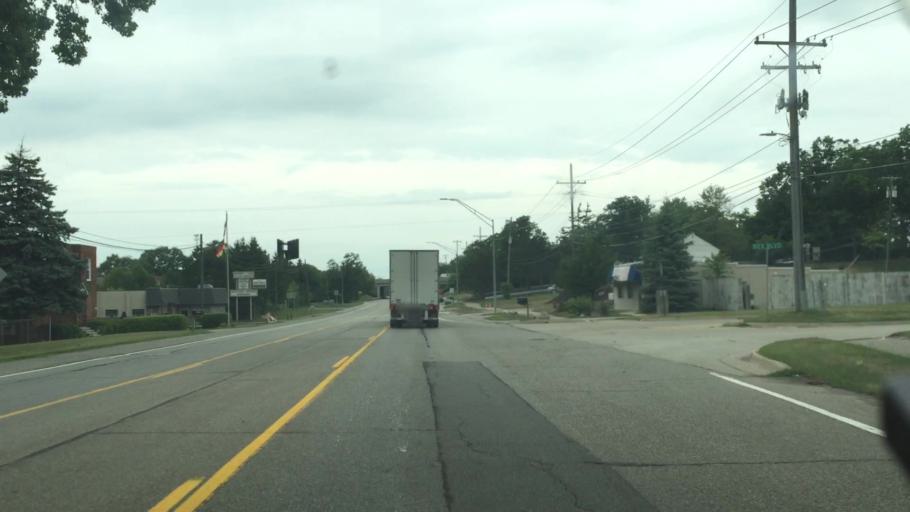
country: US
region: Michigan
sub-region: Oakland County
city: Bloomfield Hills
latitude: 42.6339
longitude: -83.2345
